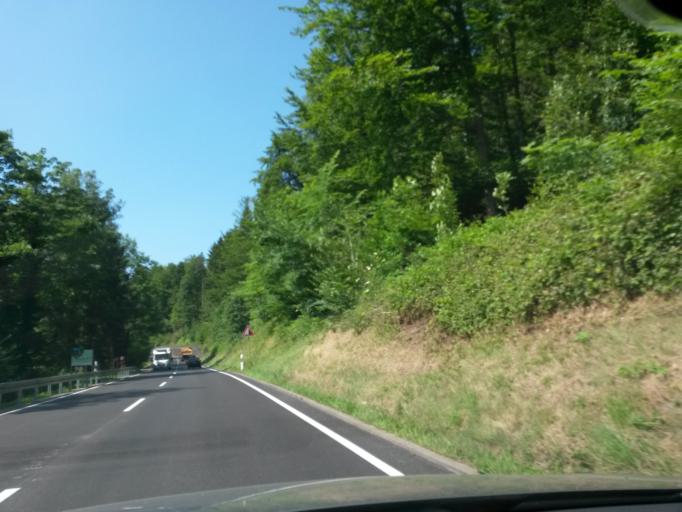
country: DE
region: Baden-Wuerttemberg
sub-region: Karlsruhe Region
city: Hofen an der Enz
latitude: 48.8105
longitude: 8.5841
